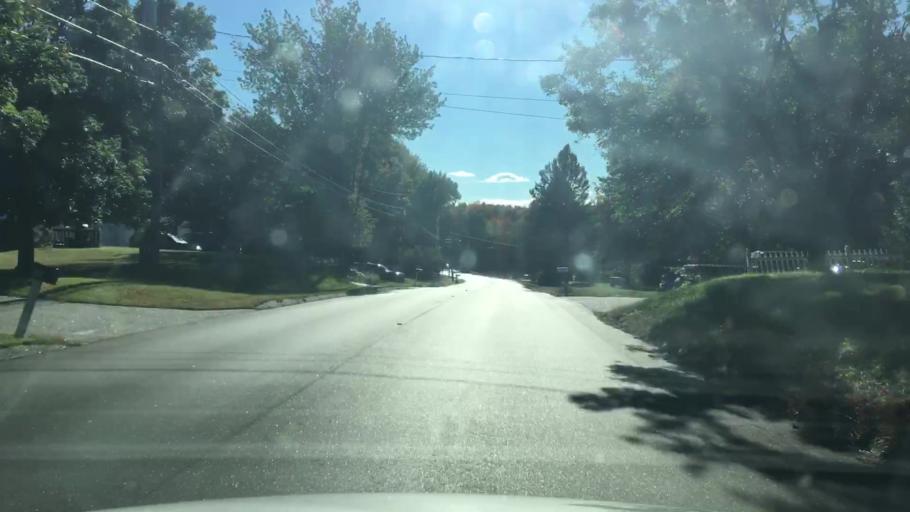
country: US
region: Maine
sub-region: Androscoggin County
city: Lisbon
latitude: 44.0716
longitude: -70.1347
